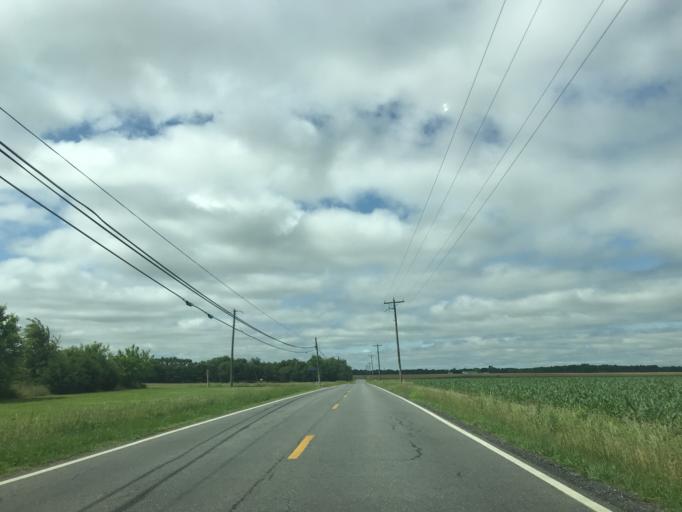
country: US
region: Maryland
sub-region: Caroline County
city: Ridgely
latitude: 38.9114
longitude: -75.9565
